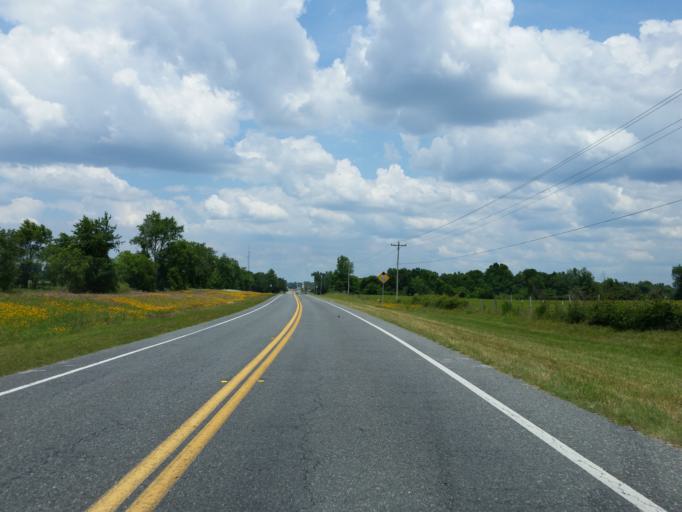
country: US
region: Florida
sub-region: Alachua County
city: High Springs
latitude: 29.9860
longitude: -82.5973
